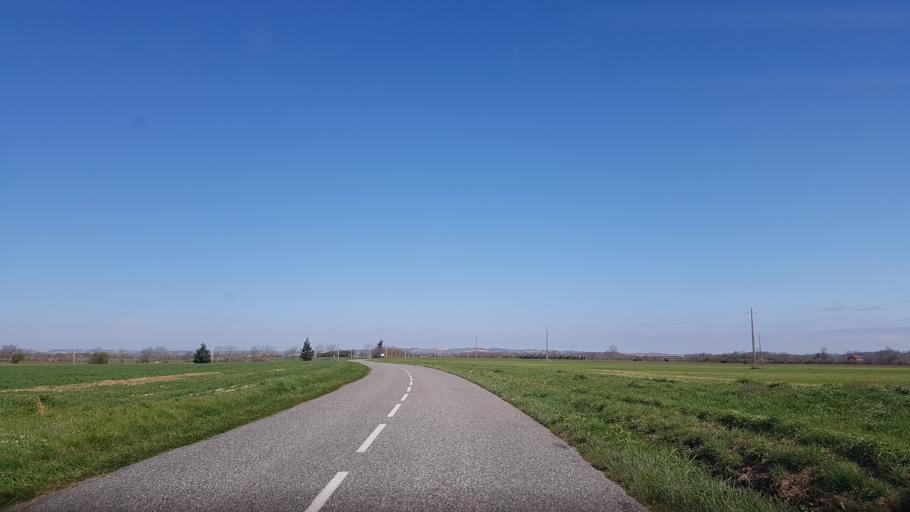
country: FR
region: Languedoc-Roussillon
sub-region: Departement de l'Aude
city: Belpech
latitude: 43.1540
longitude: 1.7064
